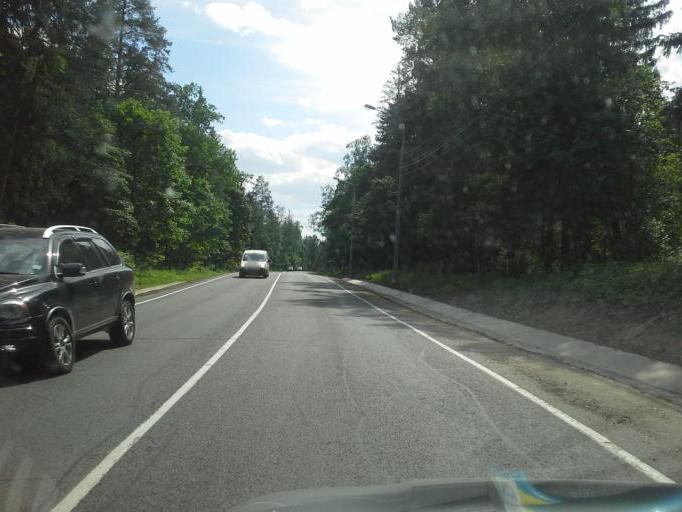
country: RU
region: Moskovskaya
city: Odintsovo
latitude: 55.7053
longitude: 37.2697
